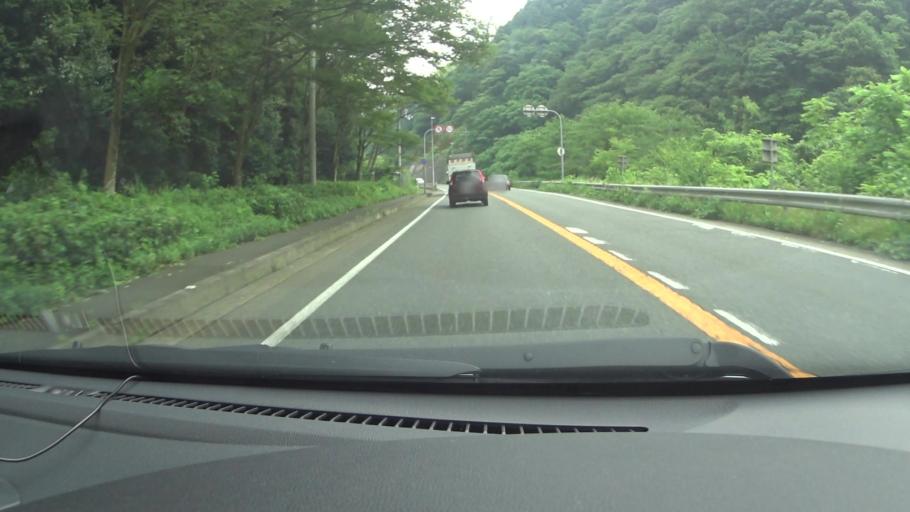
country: JP
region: Kyoto
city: Maizuru
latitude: 35.3855
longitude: 135.3135
